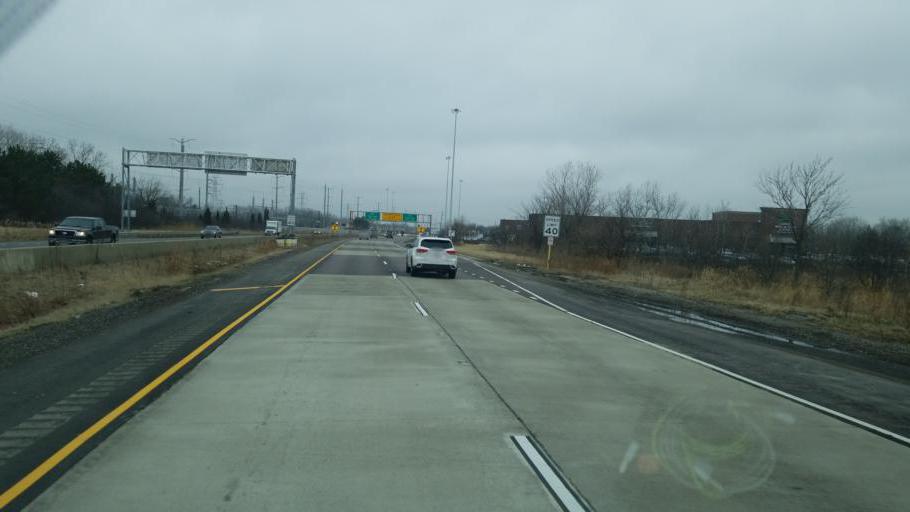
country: US
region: Illinois
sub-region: Lake County
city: Highwood
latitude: 42.1852
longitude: -87.8223
